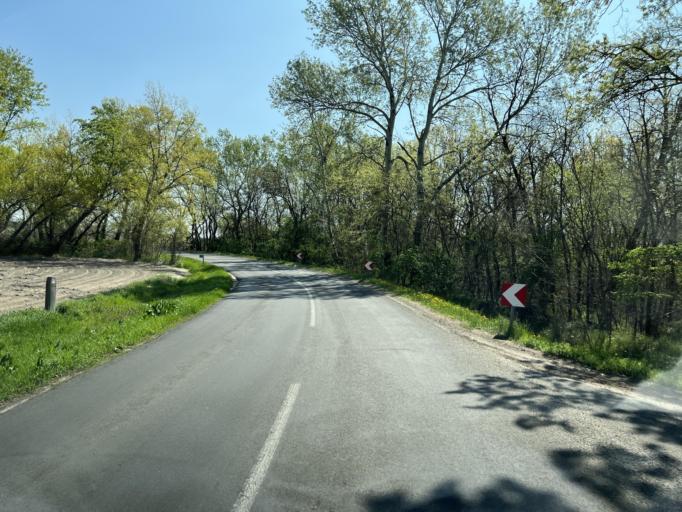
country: HU
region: Pest
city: Alsonemedi
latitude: 47.3015
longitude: 19.1872
